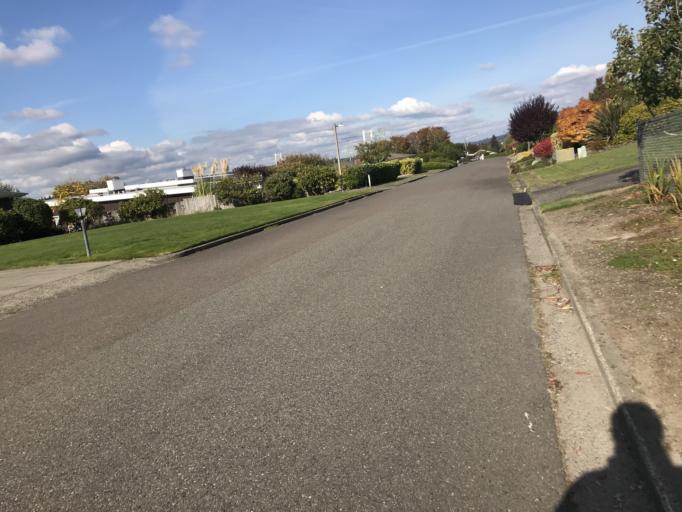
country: US
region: Washington
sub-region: Pierce County
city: University Place
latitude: 47.2504
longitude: -122.5423
